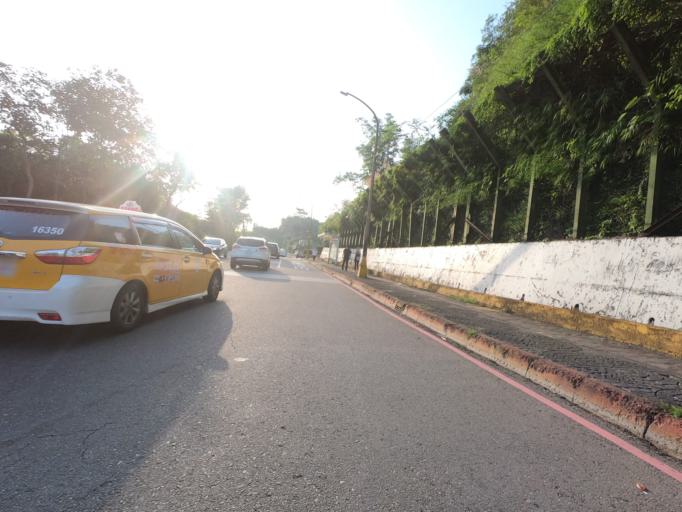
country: TW
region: Taiwan
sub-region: Keelung
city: Keelung
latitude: 25.0755
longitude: 121.6506
